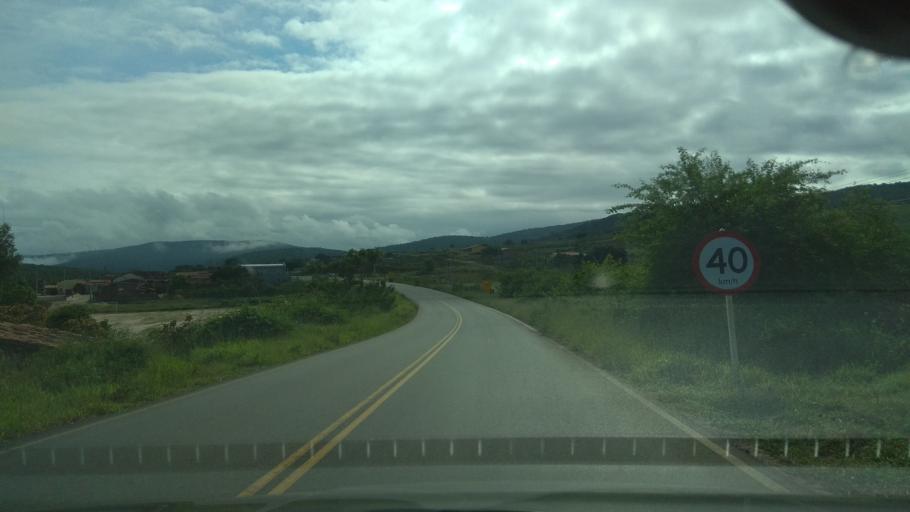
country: BR
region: Bahia
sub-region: Santa Ines
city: Santa Ines
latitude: -13.3494
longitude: -39.8748
